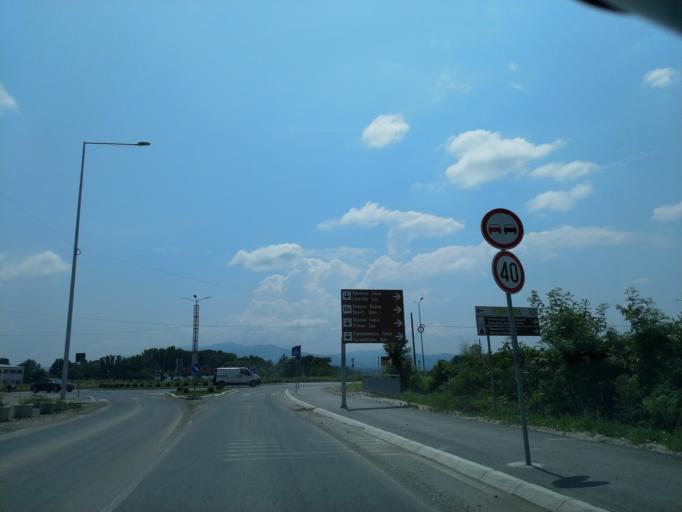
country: RS
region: Central Serbia
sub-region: Rasinski Okrug
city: Krusevac
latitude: 43.5776
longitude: 21.3510
